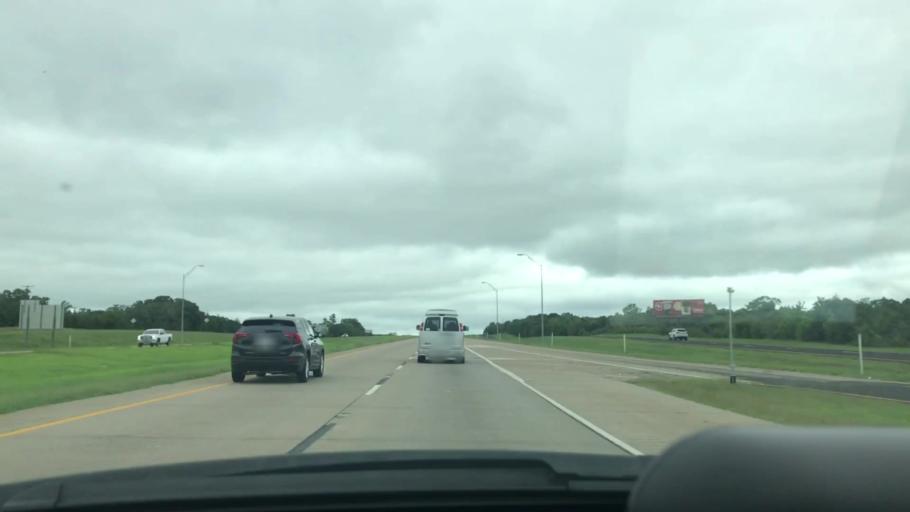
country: US
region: Texas
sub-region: Grayson County
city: Denison
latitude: 33.7328
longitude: -96.5852
